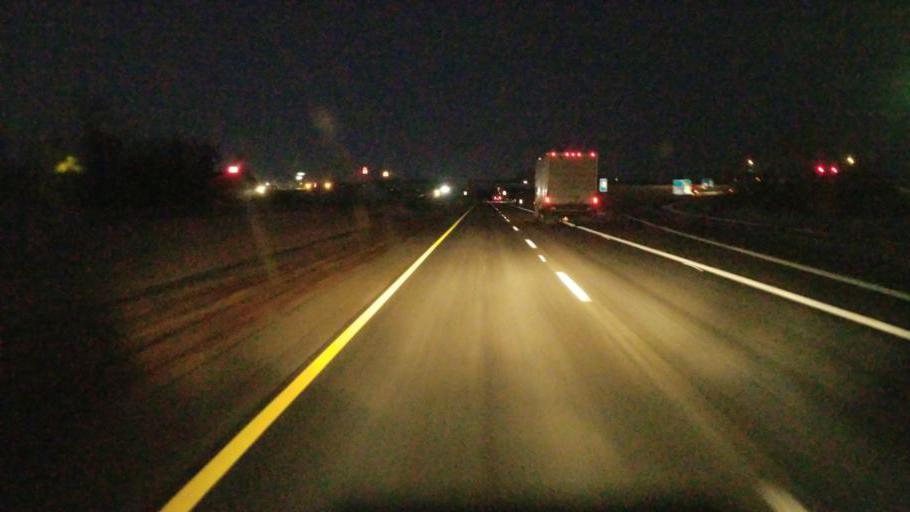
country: US
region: Ohio
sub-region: Montgomery County
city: Brookville
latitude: 39.8513
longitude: -84.4219
